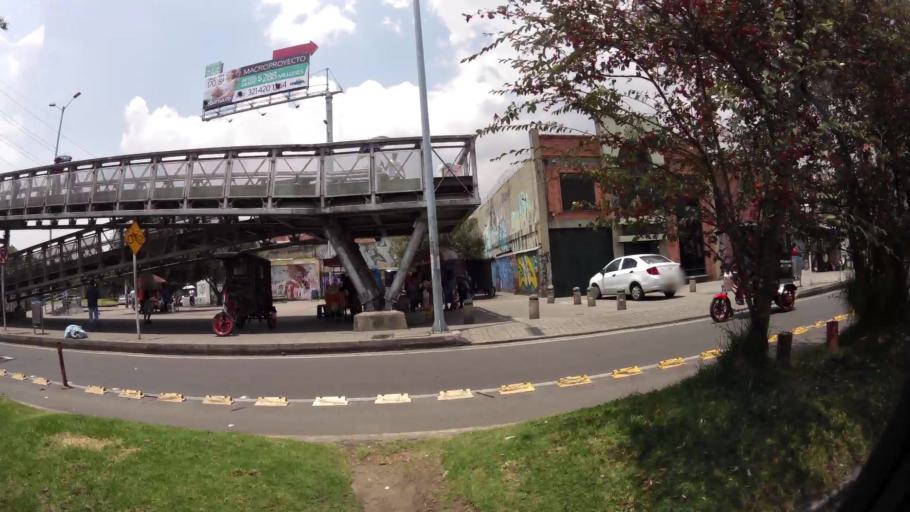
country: CO
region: Bogota D.C.
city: Barrio San Luis
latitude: 4.7418
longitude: -74.0473
